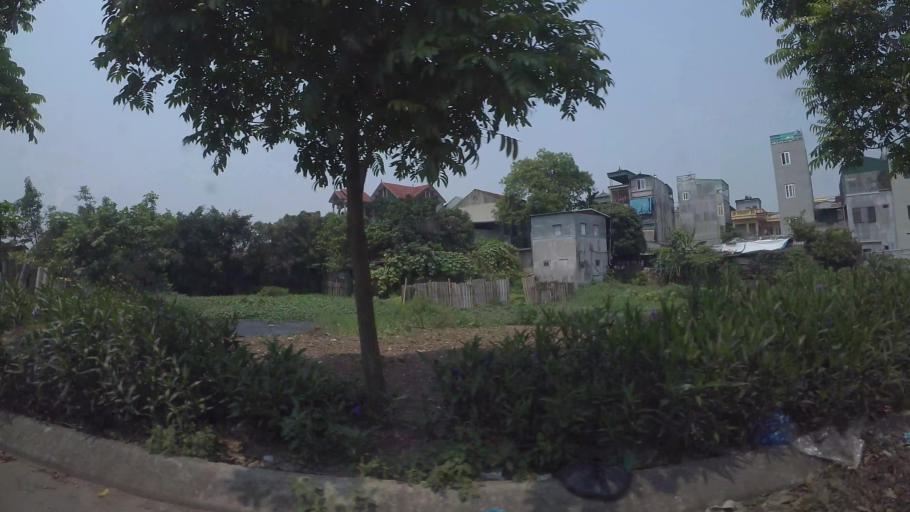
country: VN
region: Ha Noi
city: Van Dien
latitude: 20.9498
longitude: 105.8386
